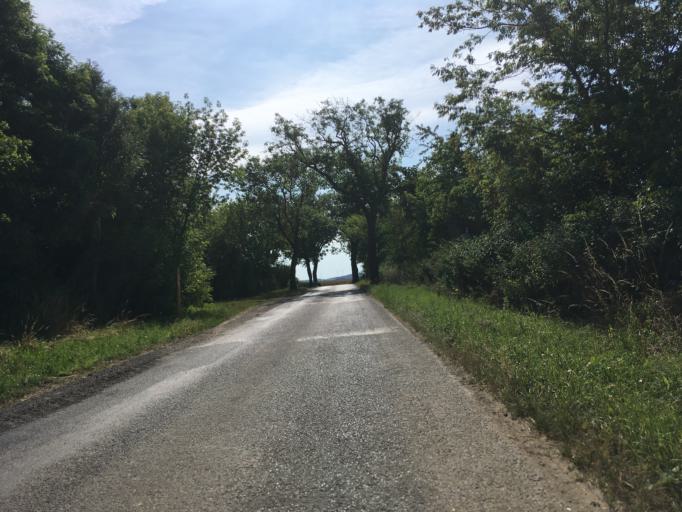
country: DE
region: Brandenburg
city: Gramzow
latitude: 53.2849
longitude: 14.0506
